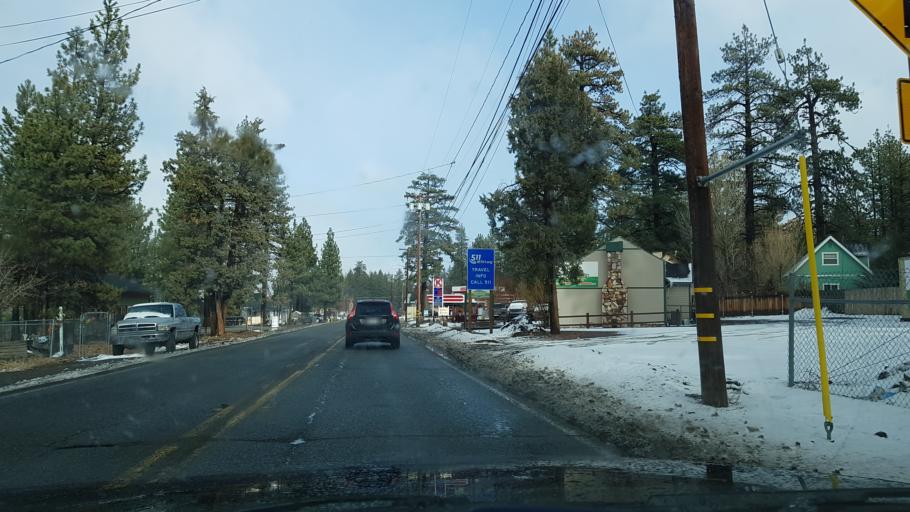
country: US
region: California
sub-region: San Bernardino County
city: Big Bear City
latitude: 34.2595
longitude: -116.8562
